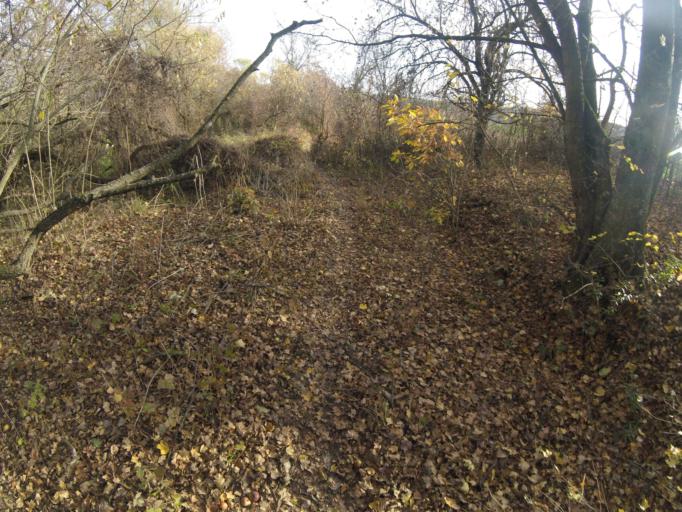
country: HU
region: Borsod-Abauj-Zemplen
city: Gonc
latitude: 48.4933
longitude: 21.4584
